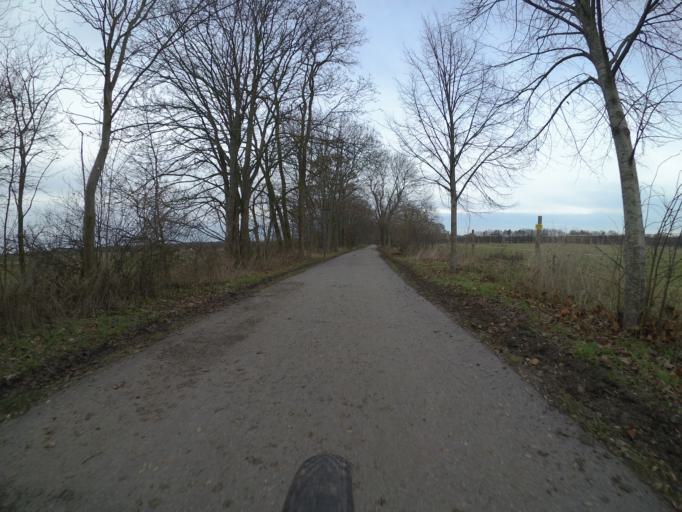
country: DE
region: Brandenburg
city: Hoppegarten
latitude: 52.4972
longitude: 13.6684
